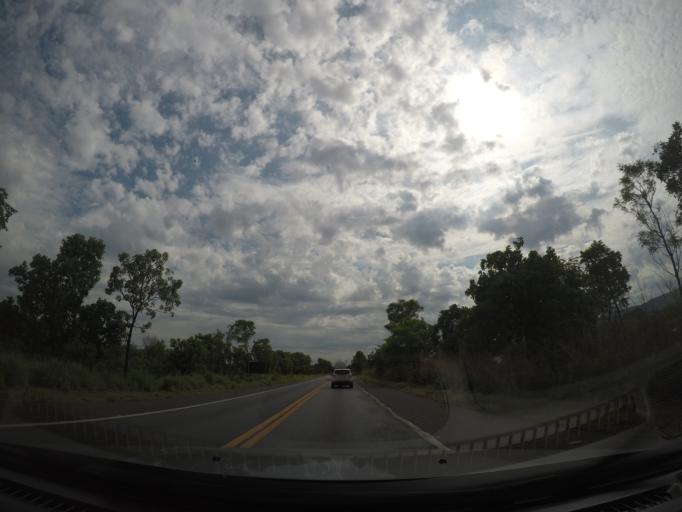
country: BR
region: Goias
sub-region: Formosa
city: Formosa
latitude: -14.9201
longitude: -46.9631
